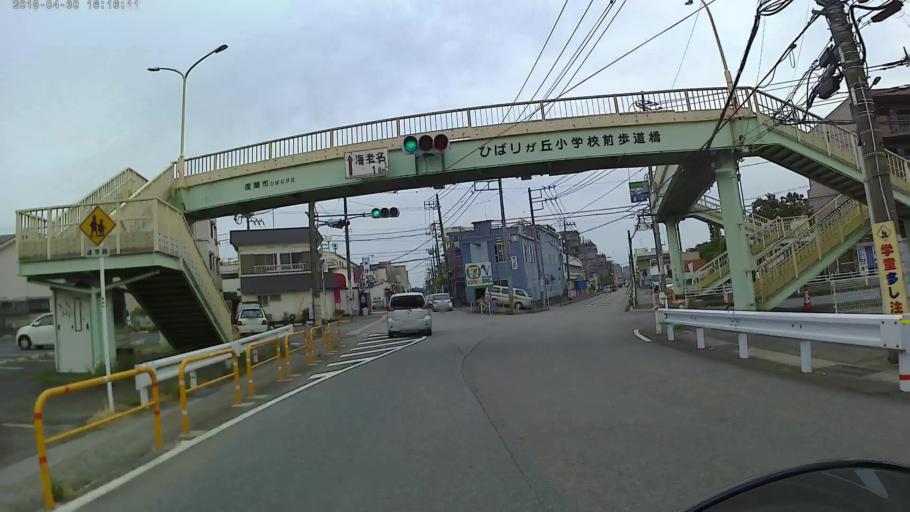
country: JP
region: Kanagawa
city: Minami-rinkan
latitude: 35.4844
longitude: 139.4316
